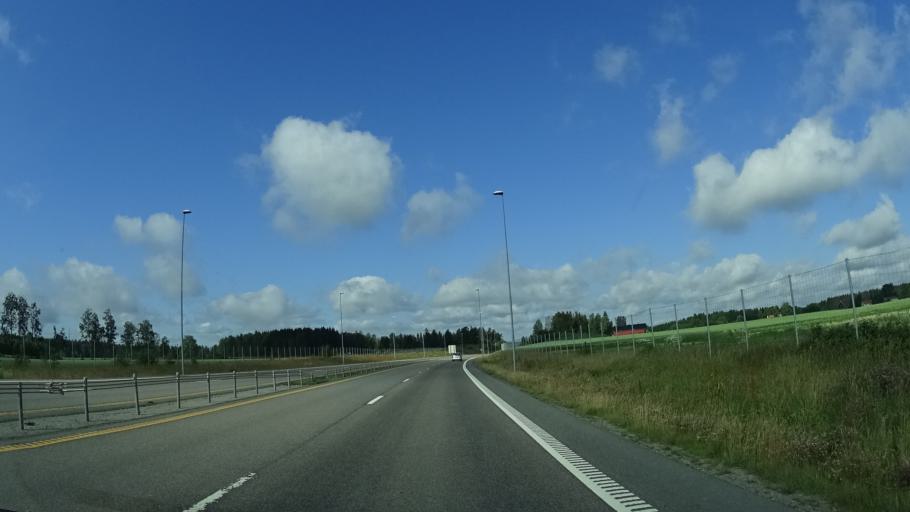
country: NO
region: Ostfold
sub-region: Askim
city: Askim
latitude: 59.5704
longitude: 11.2078
